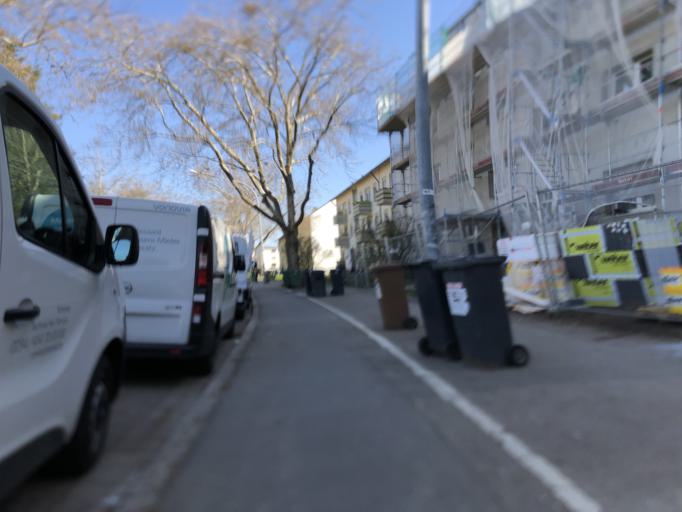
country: DE
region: Baden-Wuerttemberg
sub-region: Freiburg Region
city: Merzhausen
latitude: 47.9816
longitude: 7.8262
